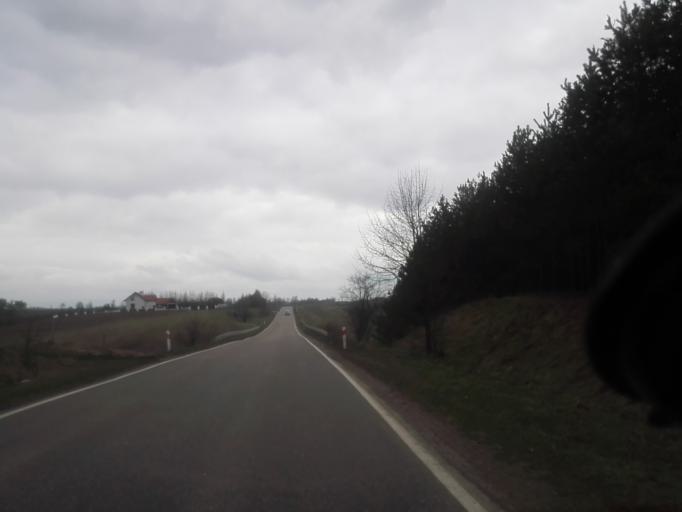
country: PL
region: Podlasie
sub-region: Suwalki
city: Suwalki
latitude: 54.2249
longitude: 22.9118
